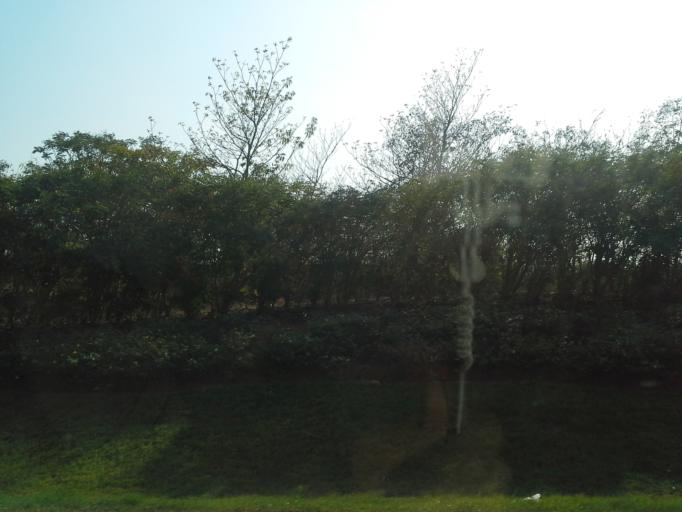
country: IN
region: Telangana
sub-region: Rangareddi
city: Balapur
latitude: 17.2438
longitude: 78.4065
